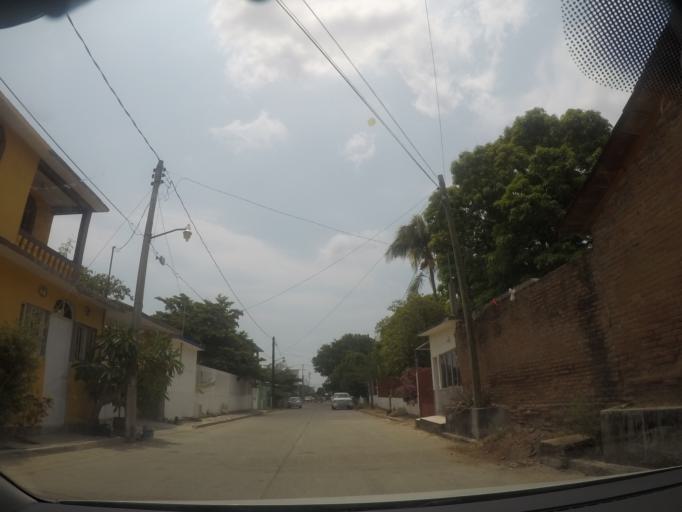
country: MX
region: Oaxaca
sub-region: El Espinal
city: El Espinal
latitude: 16.4885
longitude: -95.0457
